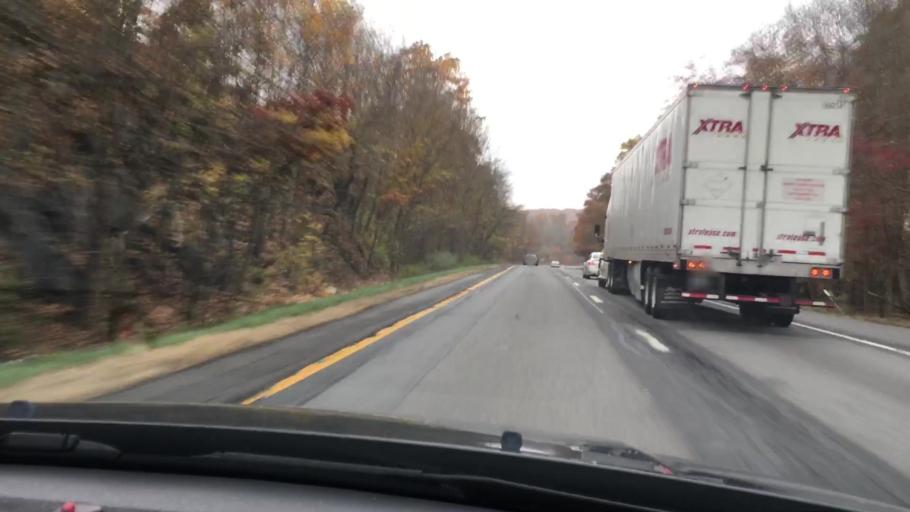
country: US
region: New York
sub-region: Putnam County
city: Lake Carmel
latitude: 41.5011
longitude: -73.6735
